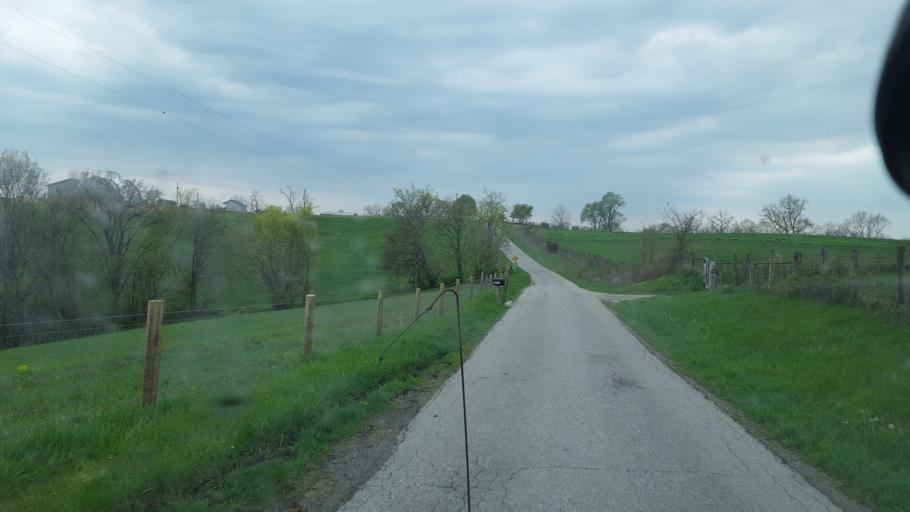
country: US
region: Kentucky
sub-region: Owen County
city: Owenton
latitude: 38.6124
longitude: -84.7675
